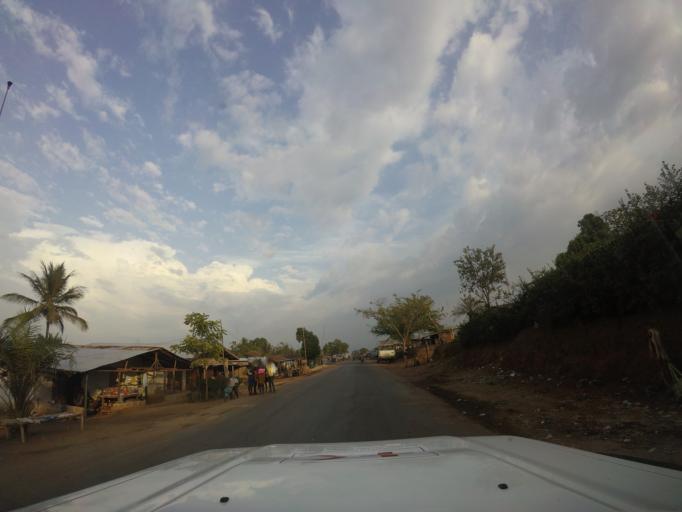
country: LR
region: Bomi
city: Tubmanburg
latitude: 6.7161
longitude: -10.9737
